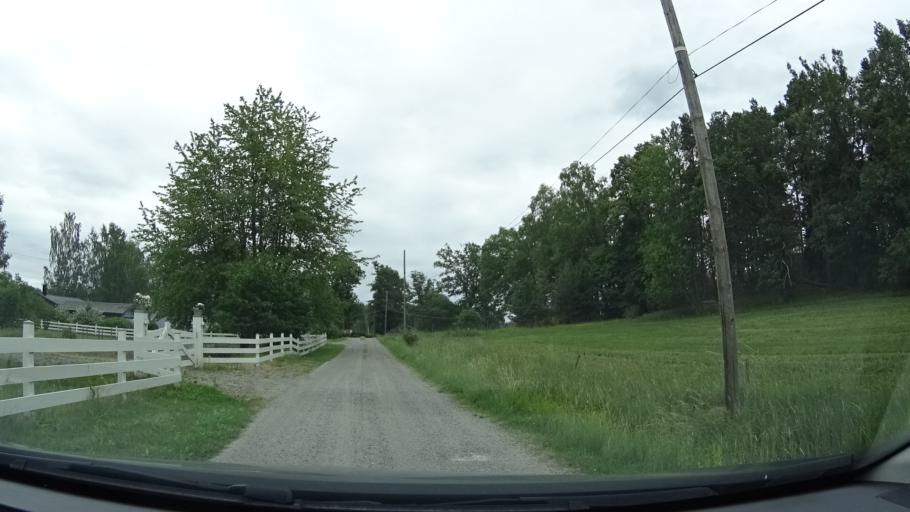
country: SE
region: Stockholm
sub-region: Varmdo Kommun
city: Mortnas
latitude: 59.3784
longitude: 18.4590
